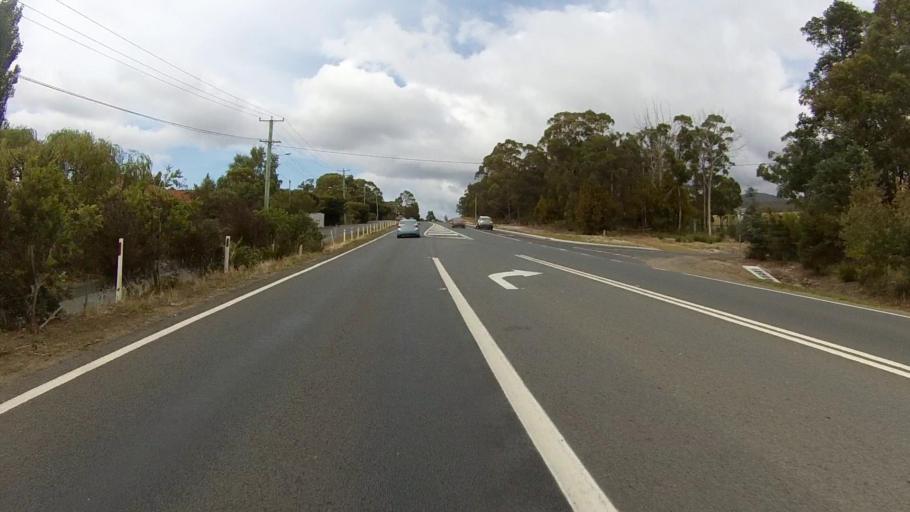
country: AU
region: Tasmania
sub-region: Kingborough
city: Margate
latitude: -43.0433
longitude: 147.2662
